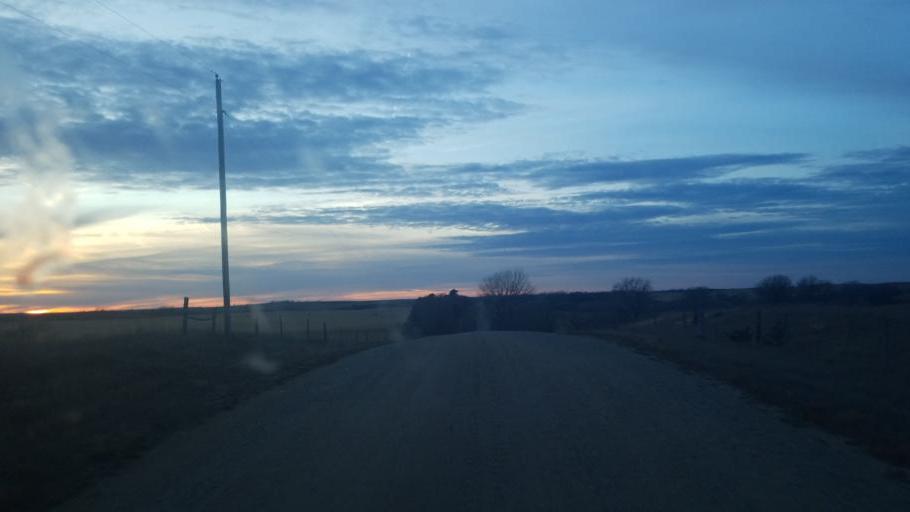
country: US
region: Nebraska
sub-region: Knox County
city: Center
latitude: 42.6554
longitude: -97.7669
